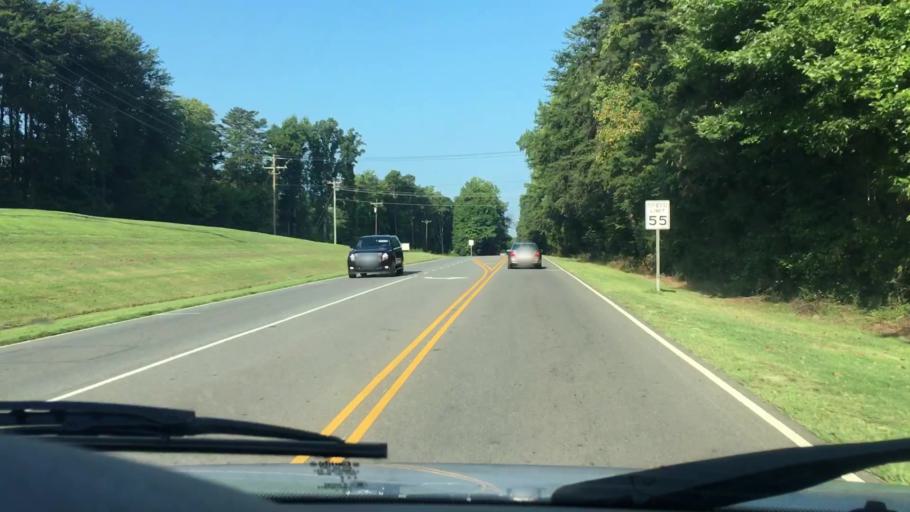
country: US
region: North Carolina
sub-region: Lincoln County
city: Lowesville
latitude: 35.4277
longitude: -80.9418
